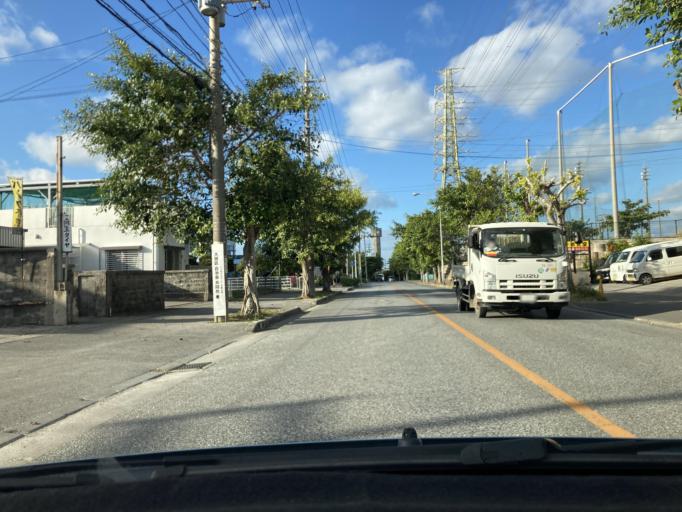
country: JP
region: Okinawa
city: Gushikawa
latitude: 26.3574
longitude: 127.8632
